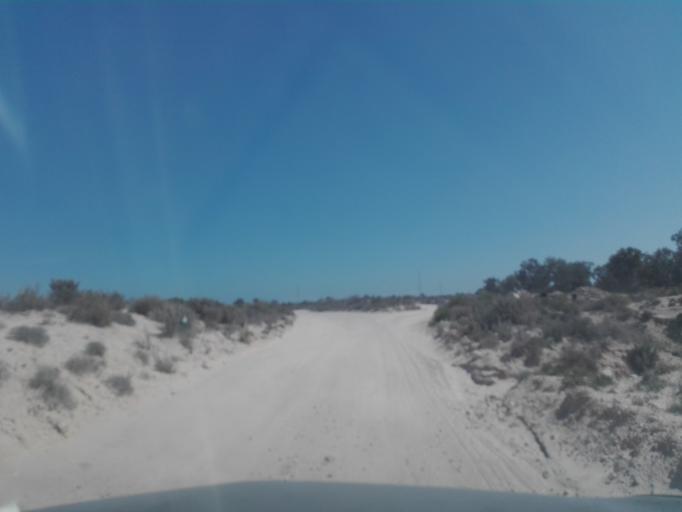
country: TN
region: Qabis
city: Gabes
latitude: 33.8747
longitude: 10.0220
